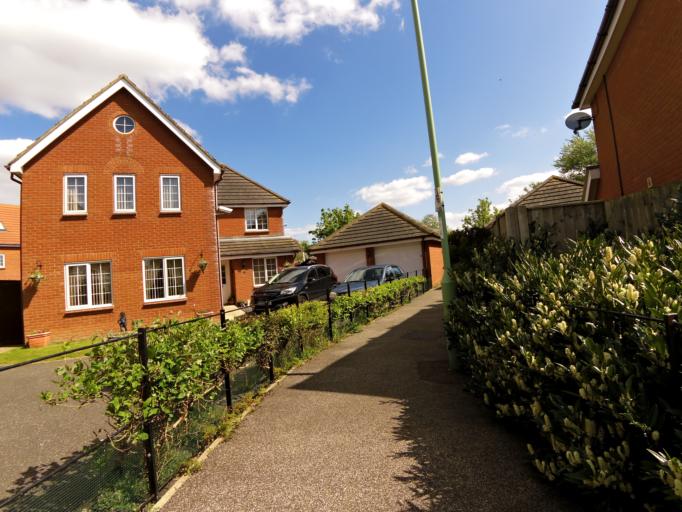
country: GB
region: England
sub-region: Suffolk
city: Kessingland
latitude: 52.4478
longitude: 1.7092
